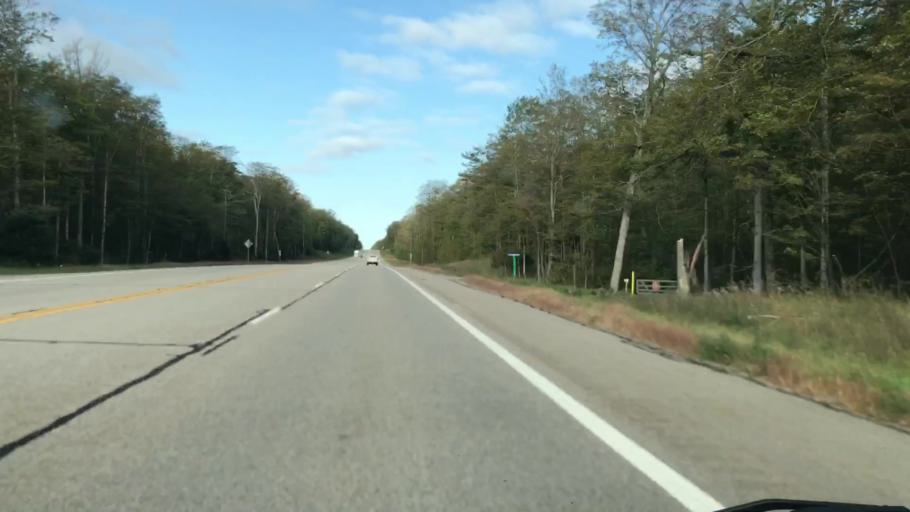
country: US
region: Michigan
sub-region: Luce County
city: Newberry
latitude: 46.3323
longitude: -85.1023
